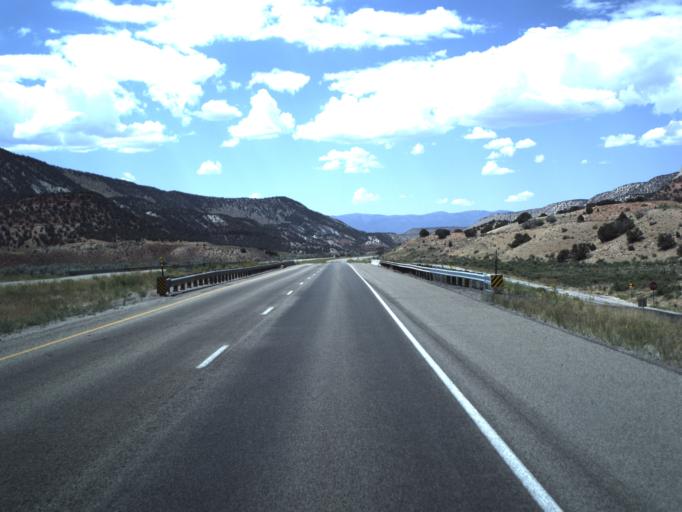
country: US
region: Utah
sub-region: Sevier County
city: Salina
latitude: 38.9164
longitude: -111.7391
